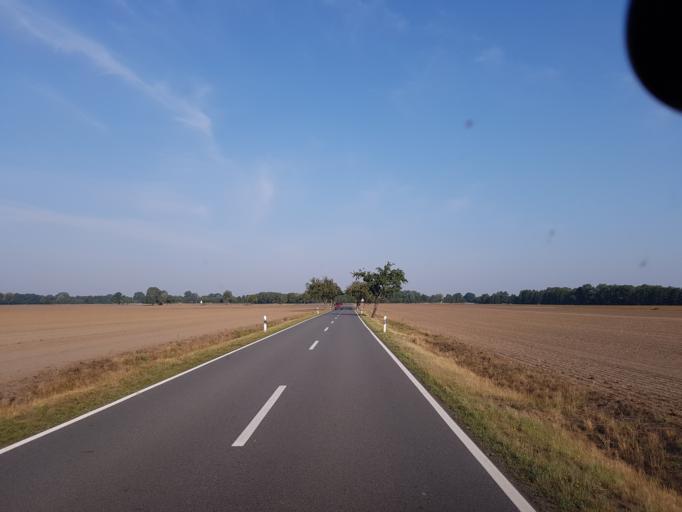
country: DE
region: Brandenburg
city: Finsterwalde
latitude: 51.6680
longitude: 13.7279
